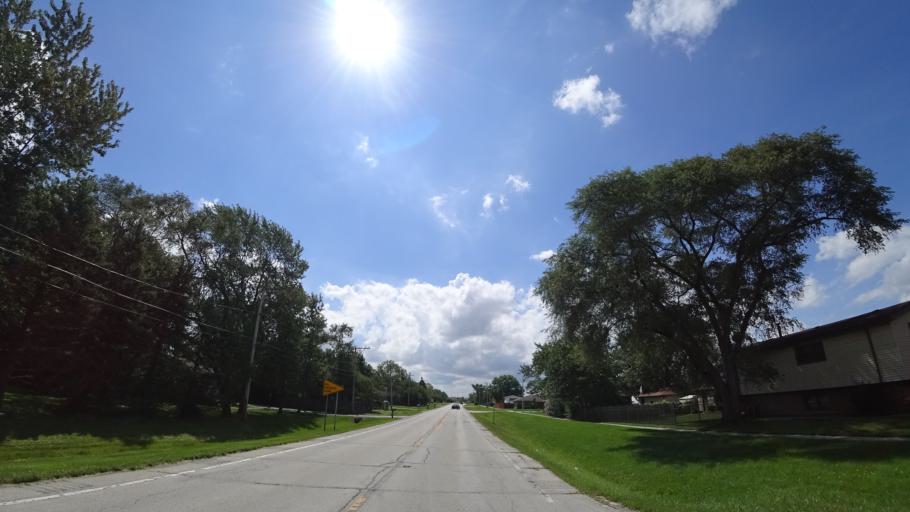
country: US
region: Illinois
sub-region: Cook County
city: Tinley Park
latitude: 41.5641
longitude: -87.7743
